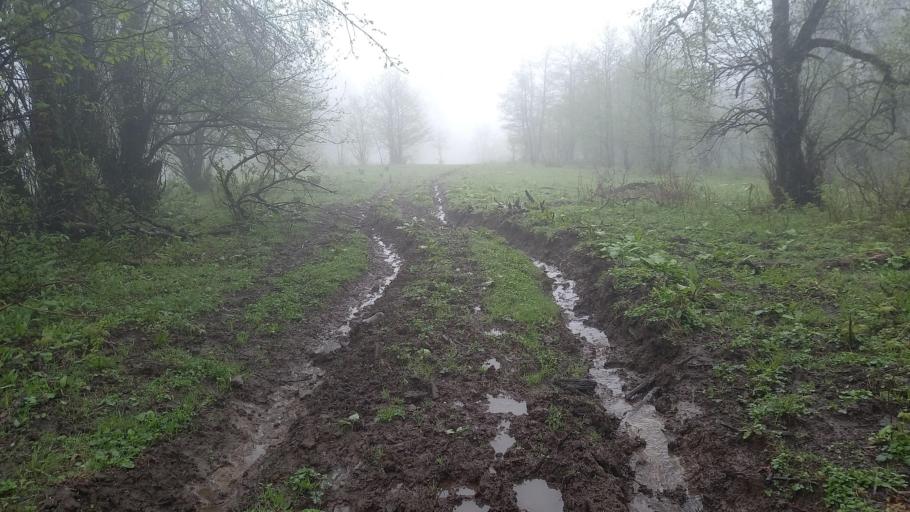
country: RU
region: Kabardino-Balkariya
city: Belaya Rechka
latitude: 43.3598
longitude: 43.4044
